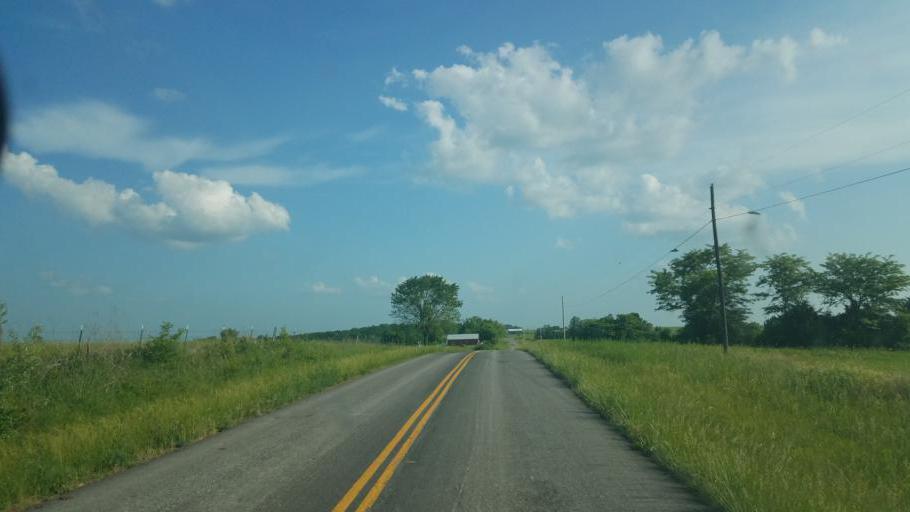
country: US
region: Missouri
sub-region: Moniteau County
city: California
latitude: 38.7725
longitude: -92.6052
